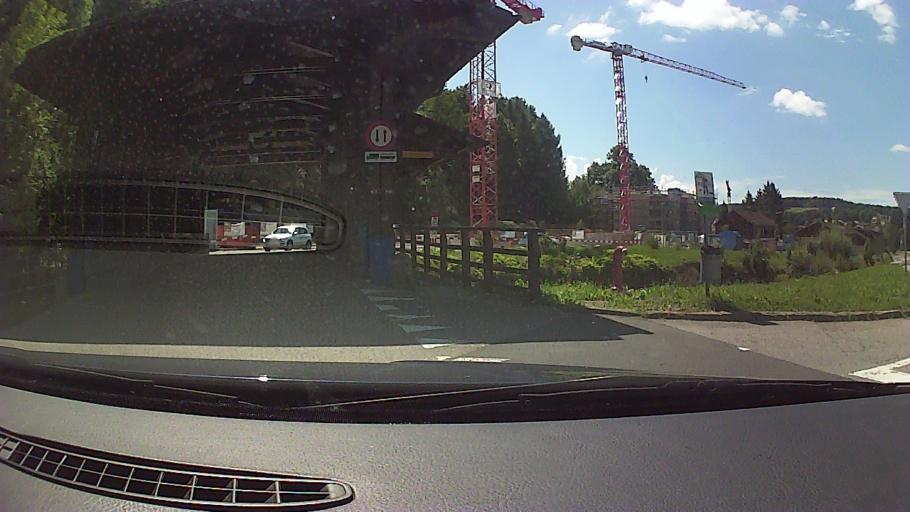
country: CH
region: Fribourg
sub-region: Veveyse District
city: Chatel-Saint-Denis
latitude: 46.5295
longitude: 6.9079
